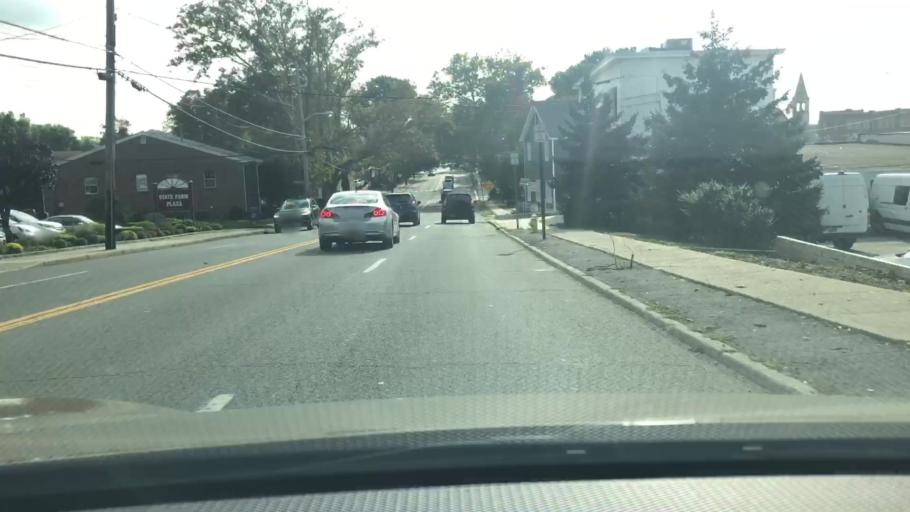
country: US
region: New York
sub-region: Westchester County
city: Tuckahoe
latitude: 40.9493
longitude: -73.8181
